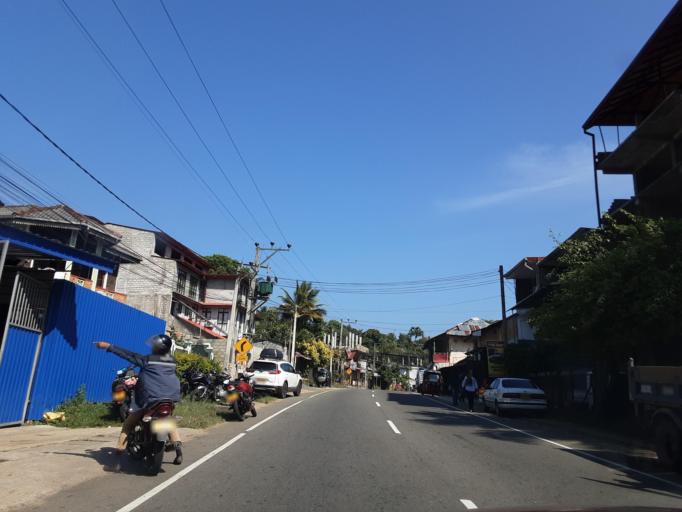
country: LK
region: Uva
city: Badulla
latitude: 7.0001
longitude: 81.0566
